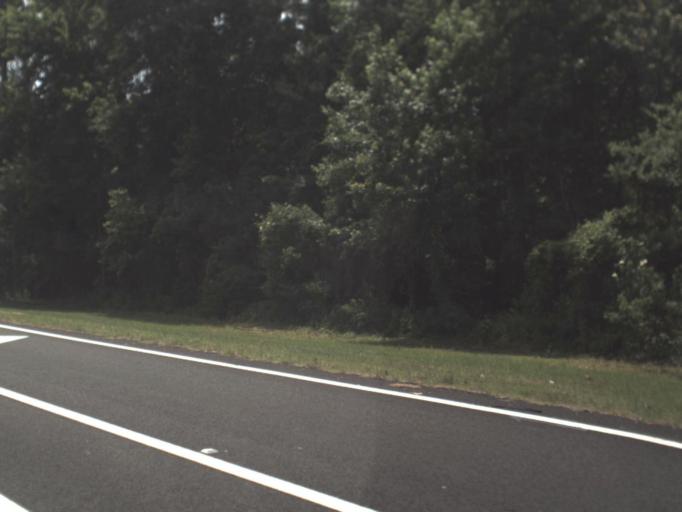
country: US
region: Florida
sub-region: Nassau County
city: Yulee
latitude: 30.6291
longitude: -81.5651
